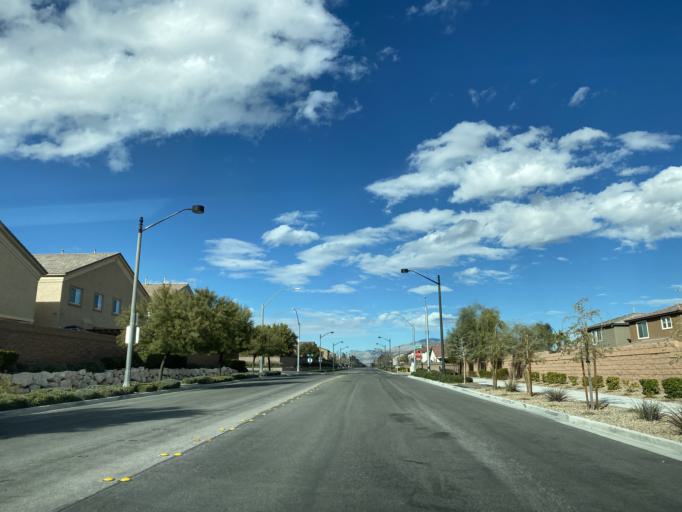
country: US
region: Nevada
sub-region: Clark County
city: Summerlin South
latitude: 36.2838
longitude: -115.3014
